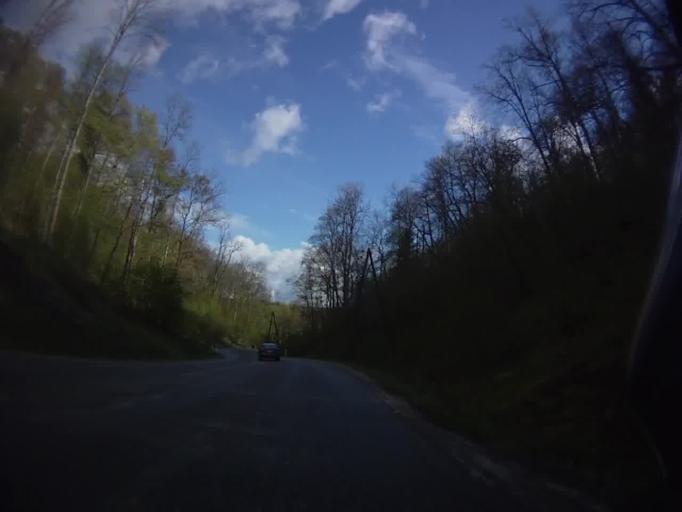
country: LV
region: Sigulda
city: Sigulda
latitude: 57.1822
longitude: 24.8485
